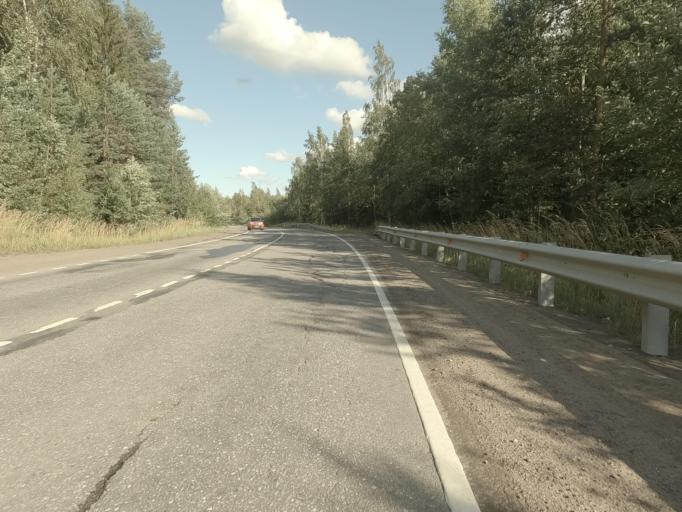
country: RU
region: Leningrad
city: Borisova Griva
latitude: 59.9854
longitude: 30.8915
